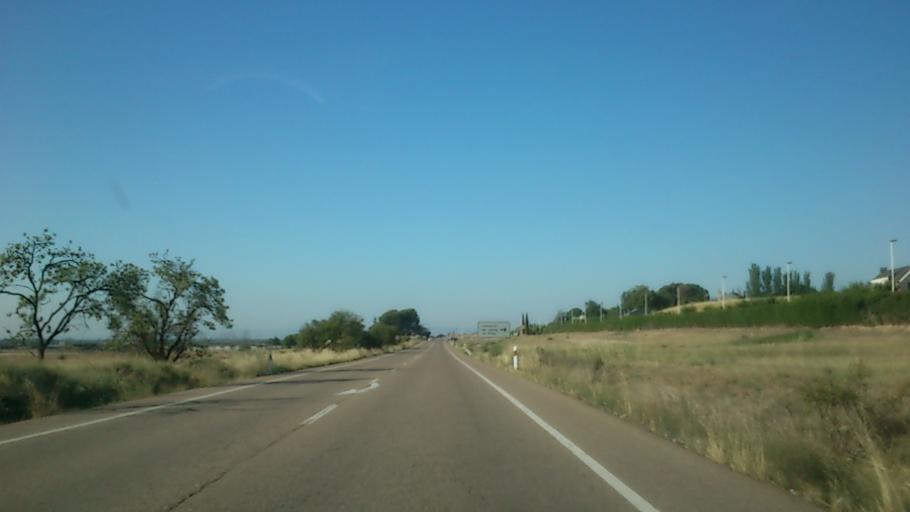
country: ES
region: Aragon
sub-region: Provincia de Zaragoza
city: Villanueva de Gallego
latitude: 41.8015
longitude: -0.8096
